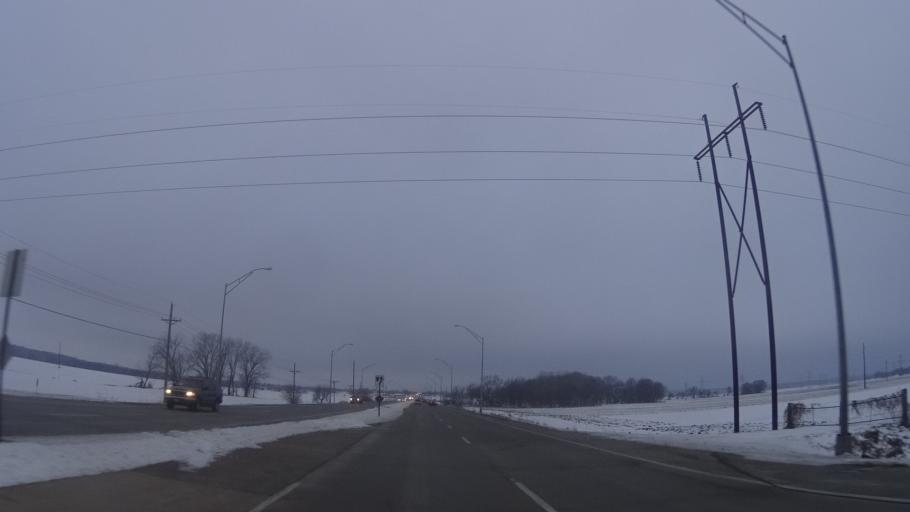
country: US
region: Nebraska
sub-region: Sarpy County
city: La Vista
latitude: 41.1619
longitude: -95.9762
